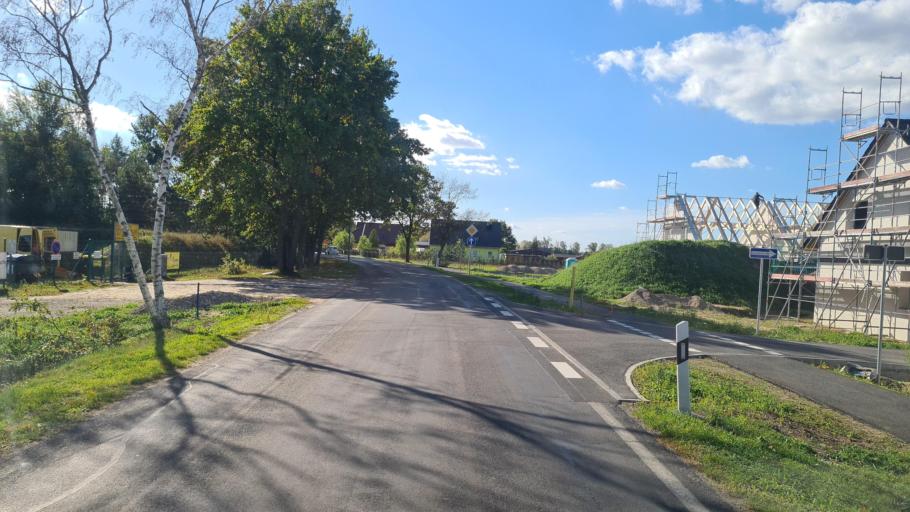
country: DE
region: Brandenburg
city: Kolkwitz
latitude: 51.7649
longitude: 14.2644
